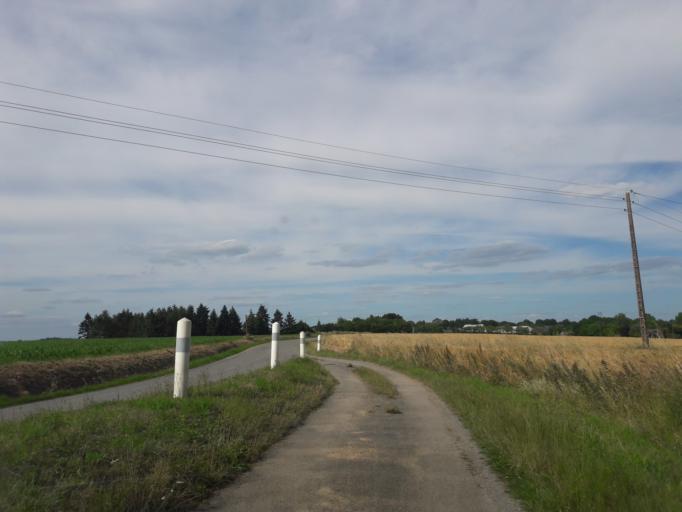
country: FR
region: Brittany
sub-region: Departement d'Ille-et-Vilaine
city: Nouvoitou
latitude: 48.0324
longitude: -1.5544
